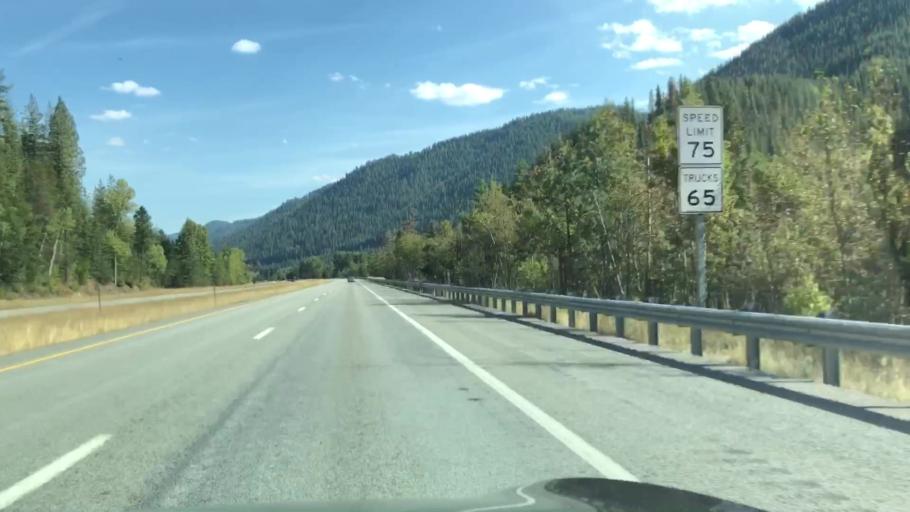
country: US
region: Idaho
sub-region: Shoshone County
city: Osburn
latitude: 47.5208
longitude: -116.0401
